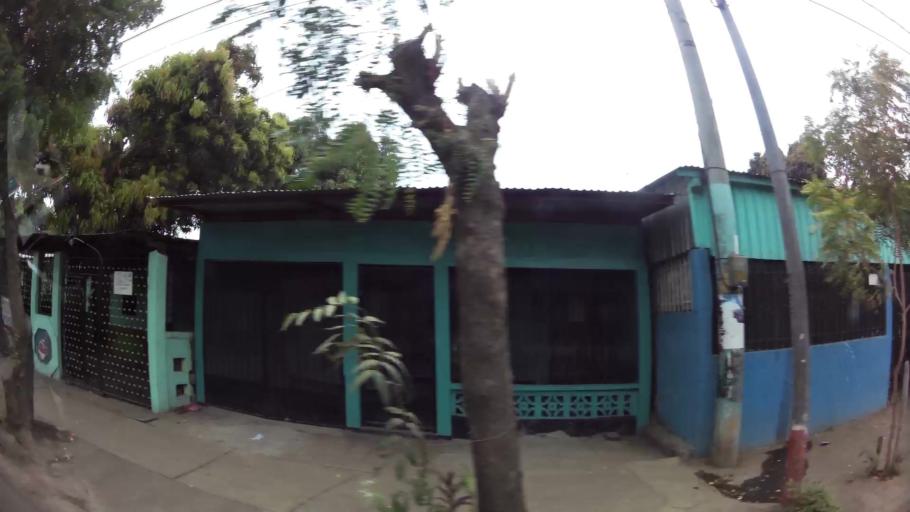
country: NI
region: Managua
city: Managua
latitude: 12.1093
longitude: -86.2316
